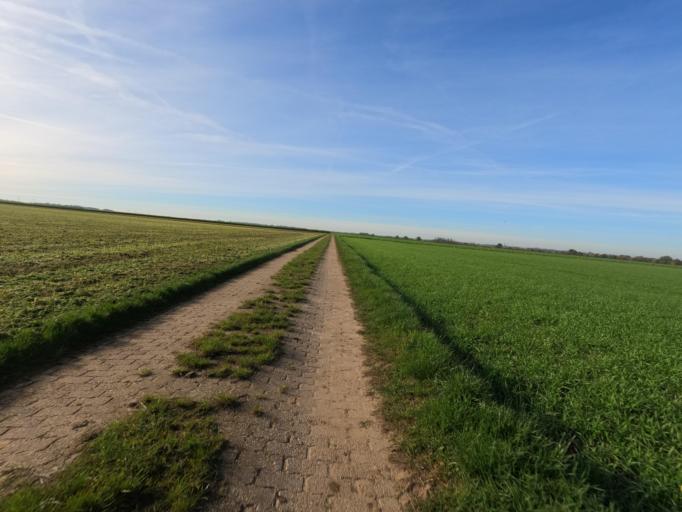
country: DE
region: North Rhine-Westphalia
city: Erkelenz
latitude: 51.0758
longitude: 6.3838
